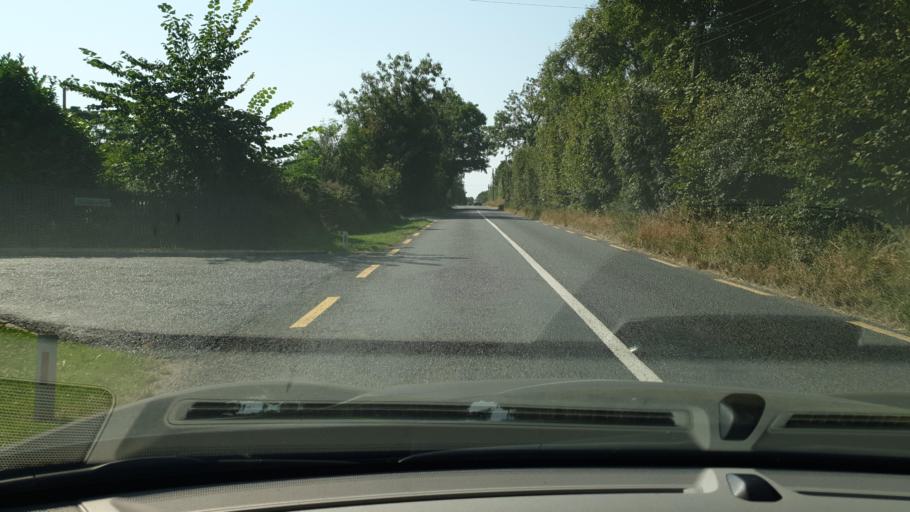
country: IE
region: Leinster
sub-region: Kildare
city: Kilcock
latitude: 53.4780
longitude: -6.7078
